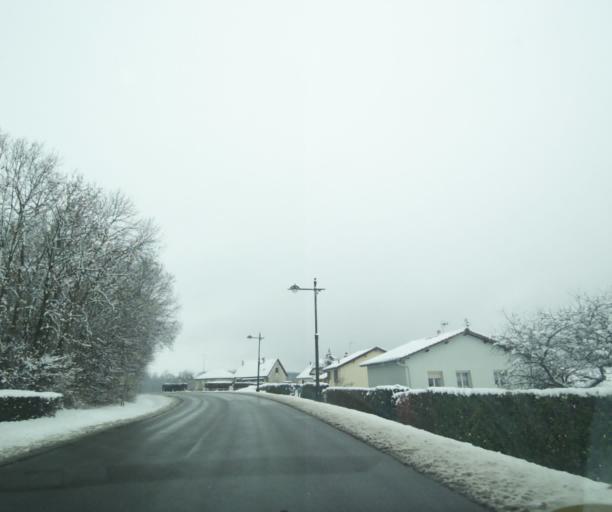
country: FR
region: Champagne-Ardenne
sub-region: Departement de la Haute-Marne
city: Montier-en-Der
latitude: 48.4842
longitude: 4.7735
